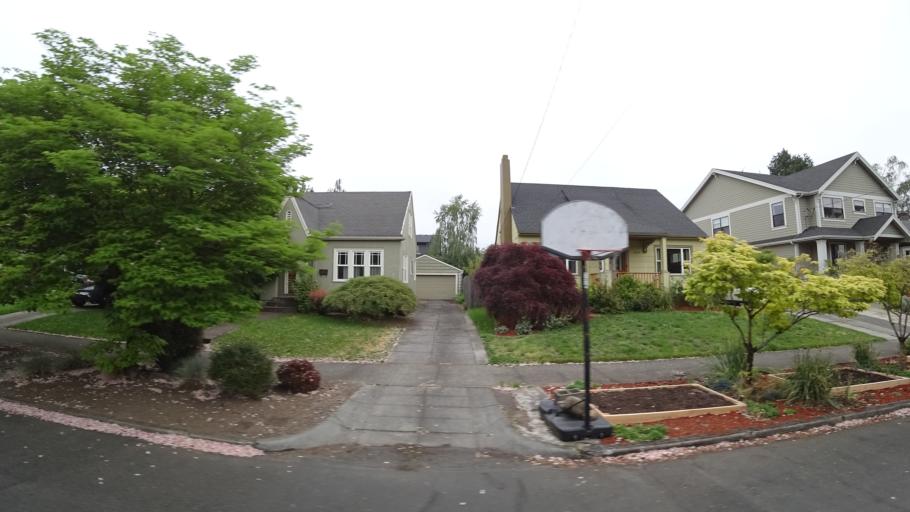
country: US
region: Oregon
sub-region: Multnomah County
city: Portland
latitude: 45.5477
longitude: -122.6239
